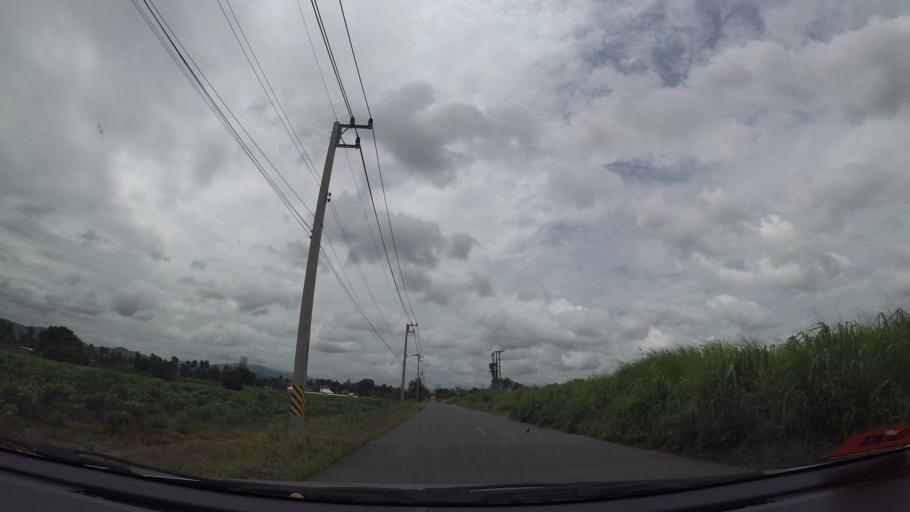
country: TH
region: Chon Buri
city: Si Racha
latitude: 13.1830
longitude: 100.9919
